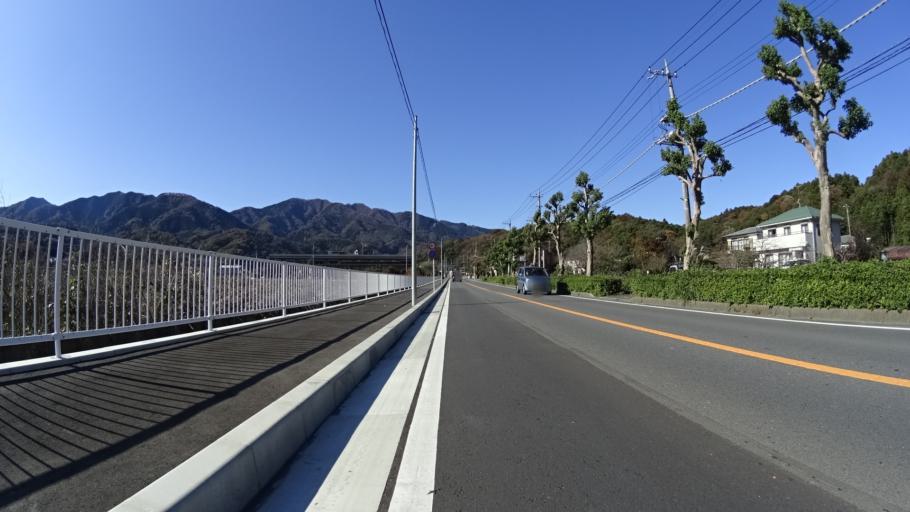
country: JP
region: Kanagawa
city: Zama
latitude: 35.5277
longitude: 139.3011
